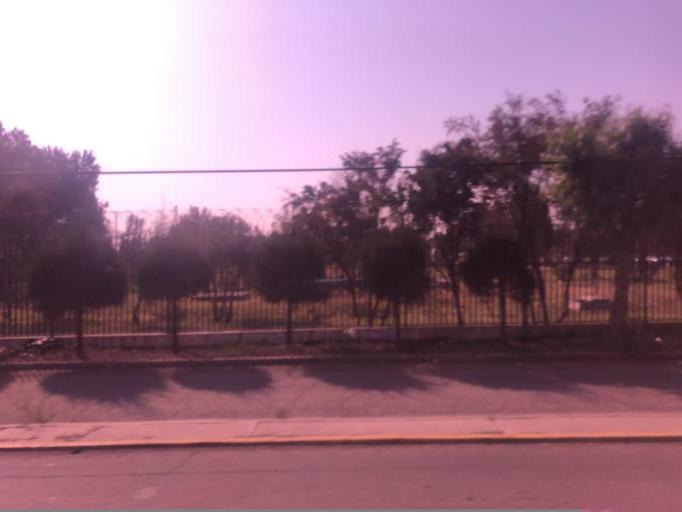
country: MX
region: Mexico
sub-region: Texcoco
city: Colonia Guadalupe Victoria
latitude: 19.4804
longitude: -98.9731
